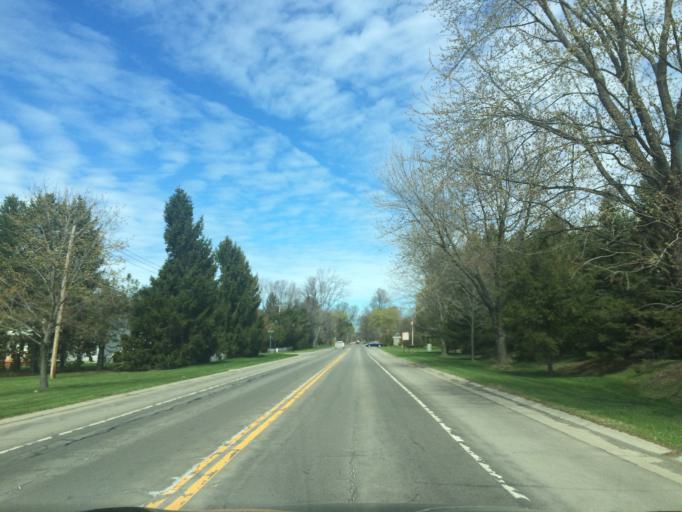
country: US
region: New York
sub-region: Monroe County
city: East Rochester
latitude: 43.0859
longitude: -77.4909
